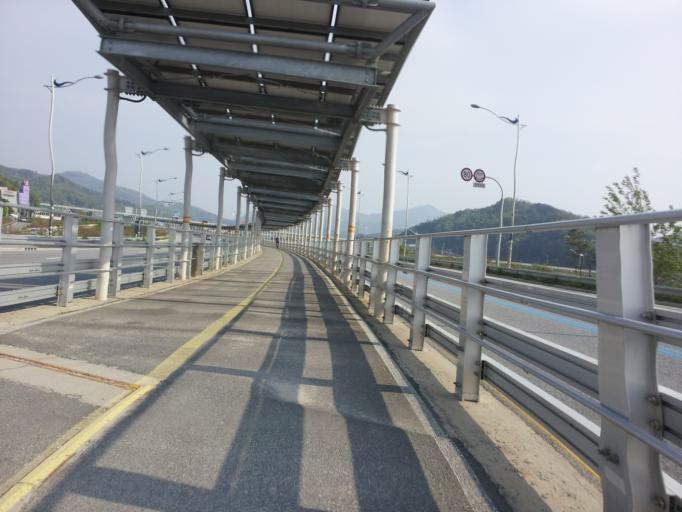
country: KR
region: Daejeon
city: Songgang-dong
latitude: 36.4647
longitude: 127.2755
